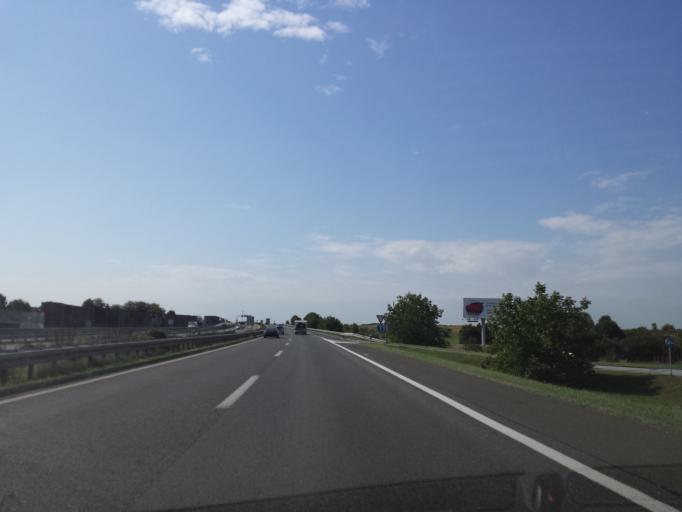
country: HR
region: Grad Zagreb
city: Brezovica
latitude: 45.7449
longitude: 15.8811
